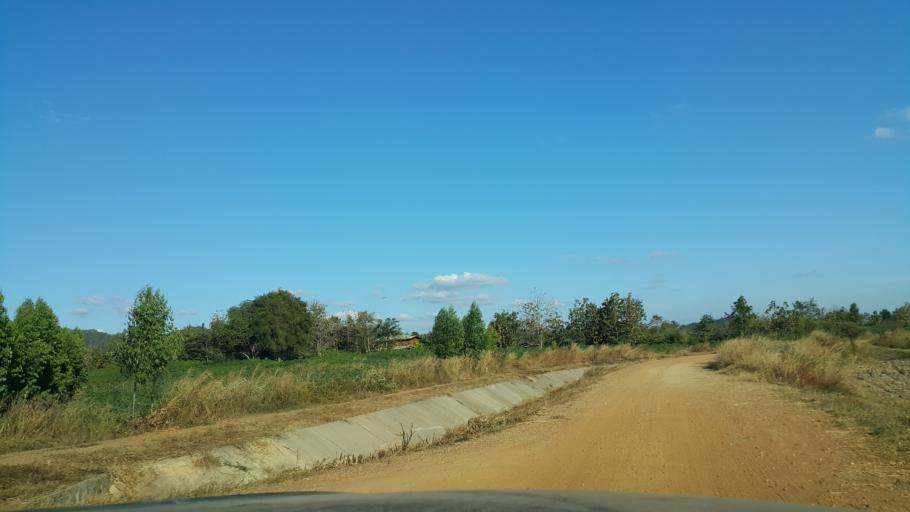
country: TH
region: Sukhothai
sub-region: Amphoe Si Satchanalai
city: Si Satchanalai
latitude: 17.4739
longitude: 99.6576
